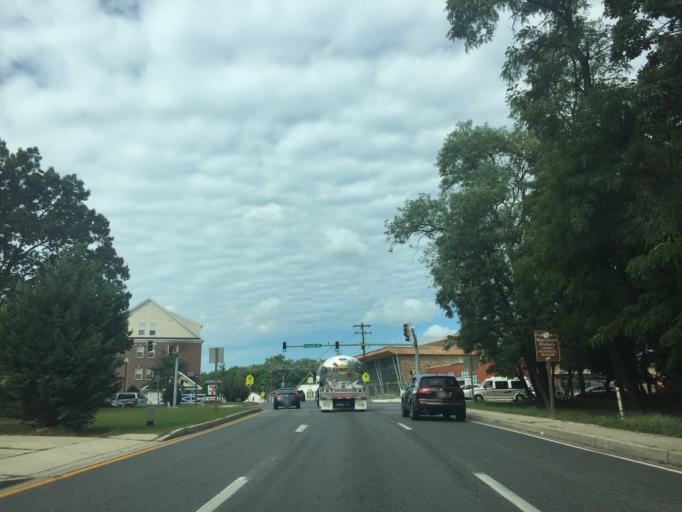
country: US
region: Maryland
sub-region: Prince George's County
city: Laurel
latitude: 39.1030
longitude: -76.8550
